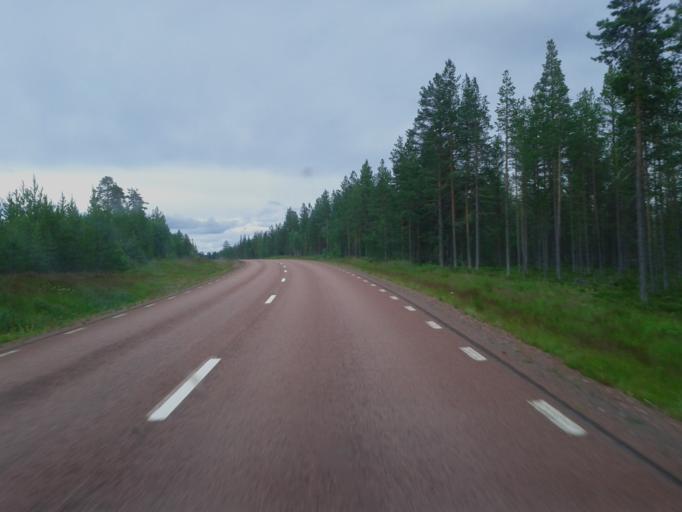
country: SE
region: Dalarna
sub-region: Alvdalens Kommun
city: AElvdalen
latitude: 61.5542
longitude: 13.3219
